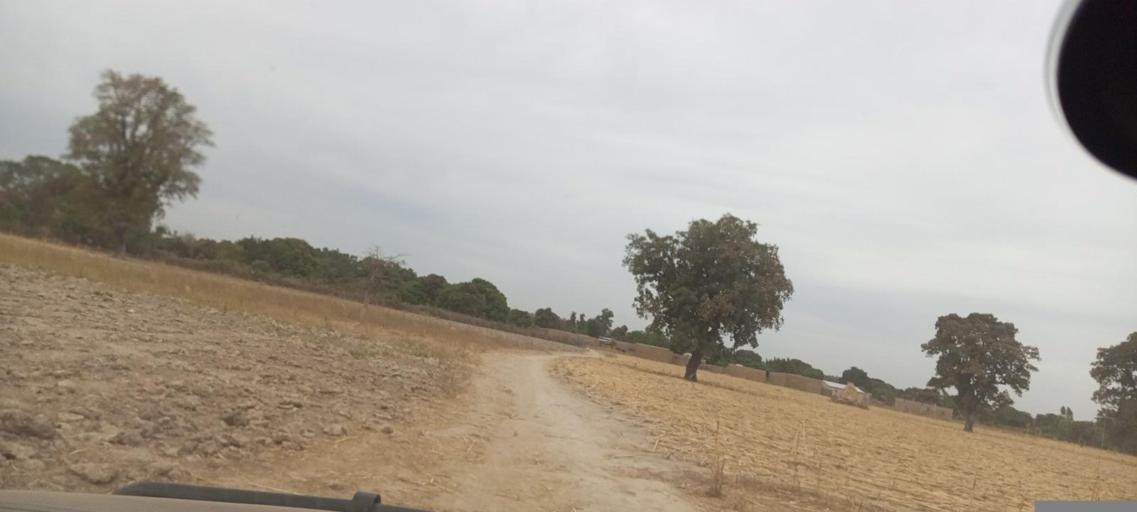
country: ML
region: Koulikoro
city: Kati
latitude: 12.7403
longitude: -8.3290
